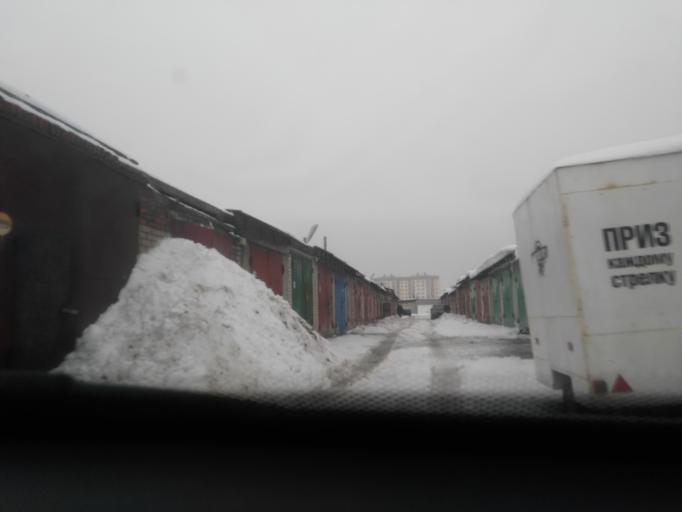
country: BY
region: Mogilev
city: Babruysk
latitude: 53.1930
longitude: 29.2160
